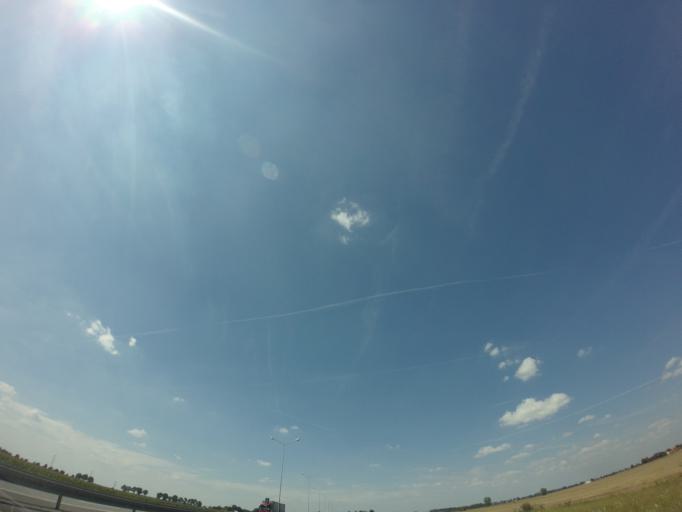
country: PL
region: Lower Silesian Voivodeship
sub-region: Powiat wroclawski
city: Zorawina
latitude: 50.9507
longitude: 17.0845
